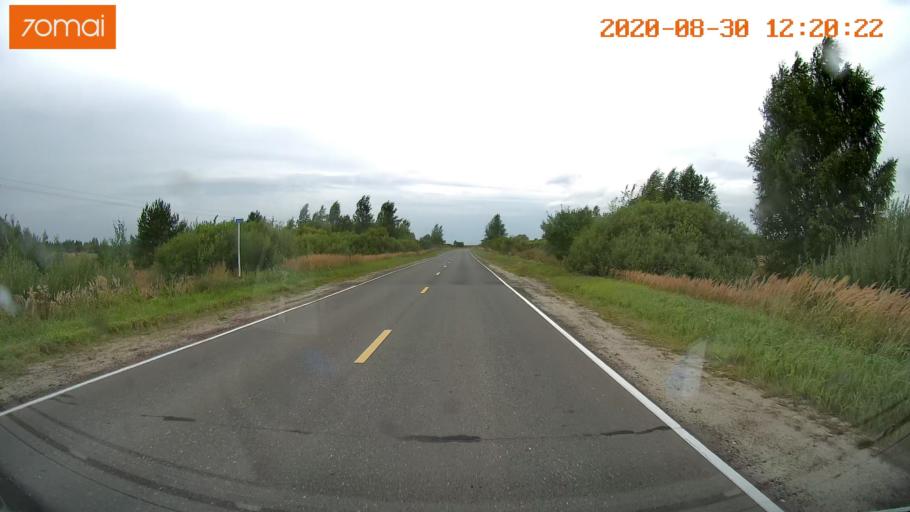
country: RU
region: Ivanovo
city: Yur'yevets
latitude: 57.3228
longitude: 42.9026
